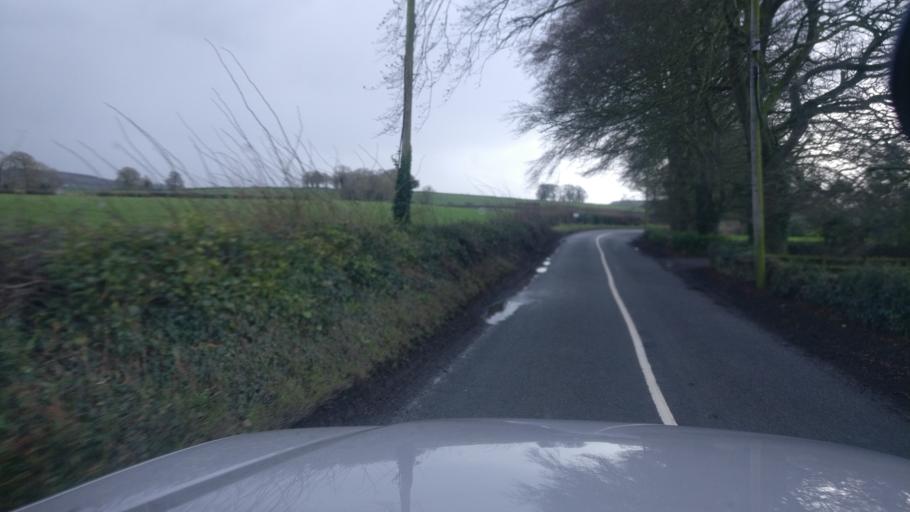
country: IE
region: Munster
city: Nenagh Bridge
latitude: 52.9730
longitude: -8.0900
